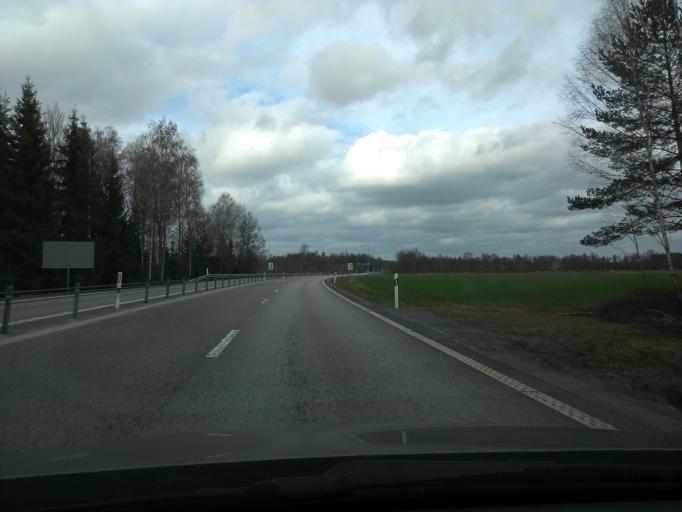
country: SE
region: Kronoberg
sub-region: Alvesta Kommun
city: Vislanda
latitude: 56.7743
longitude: 14.5438
